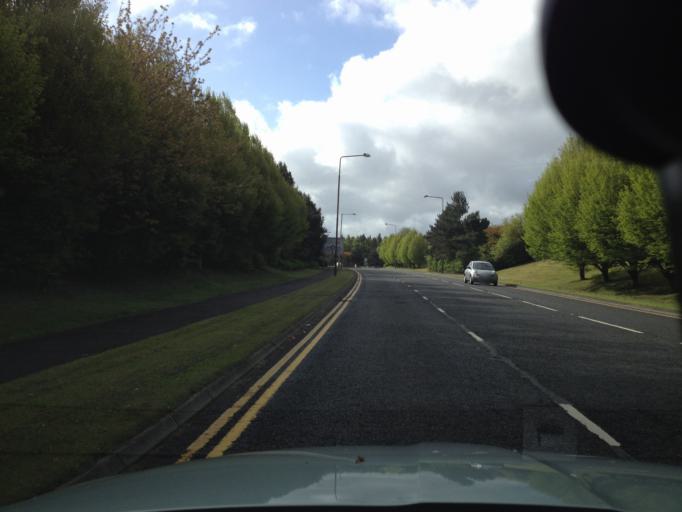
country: GB
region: Scotland
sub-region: West Lothian
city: Livingston
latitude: 55.8737
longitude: -3.5257
